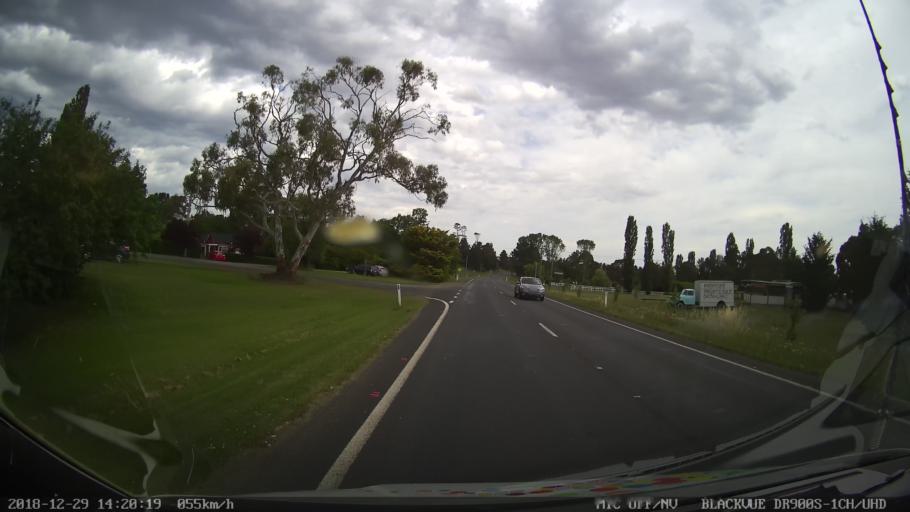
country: AU
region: New South Wales
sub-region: Cooma-Monaro
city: Cooma
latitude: -36.5071
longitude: 149.2853
